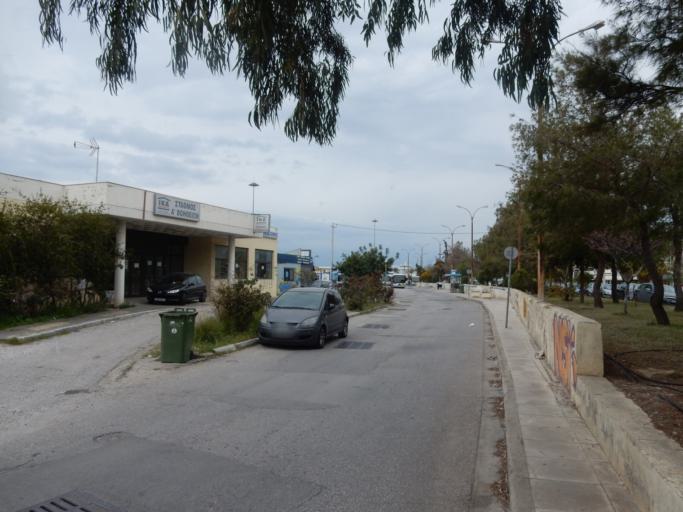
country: GR
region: Attica
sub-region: Nomos Piraios
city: Perama
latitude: 37.9639
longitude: 23.5601
